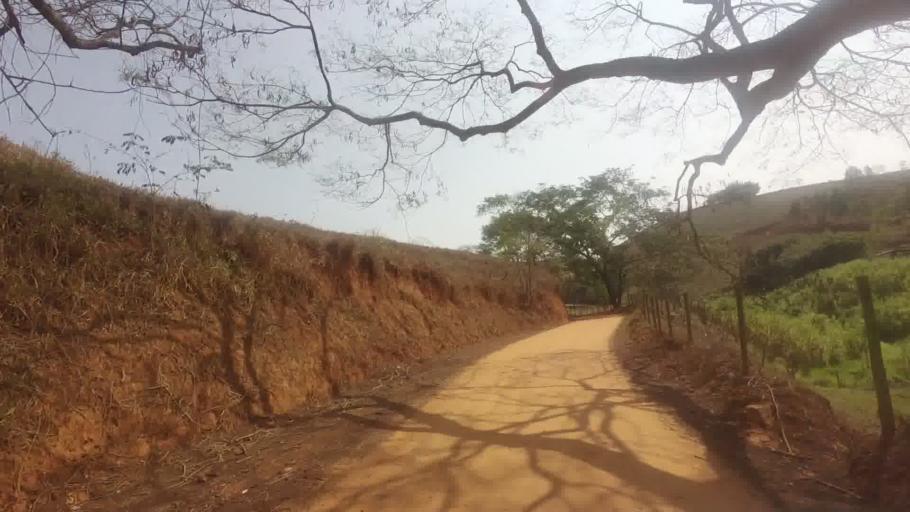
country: BR
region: Espirito Santo
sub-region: Sao Jose Do Calcado
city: Sao Jose do Calcado
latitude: -21.0689
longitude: -41.5505
